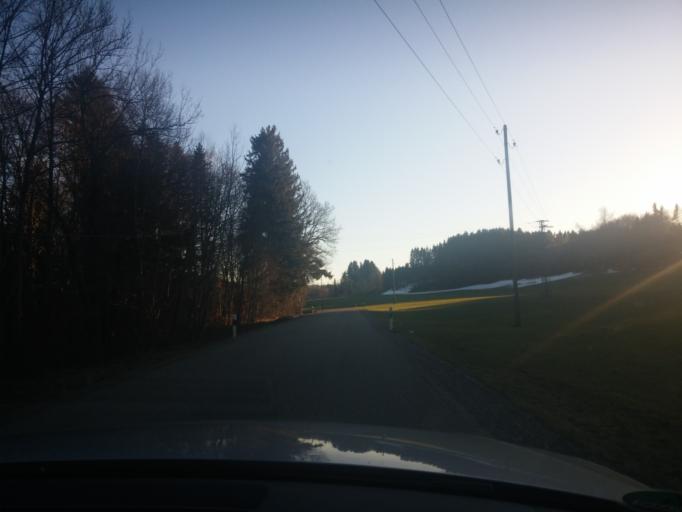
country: DE
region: Bavaria
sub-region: Swabia
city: Altusried
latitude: 47.8219
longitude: 10.1773
